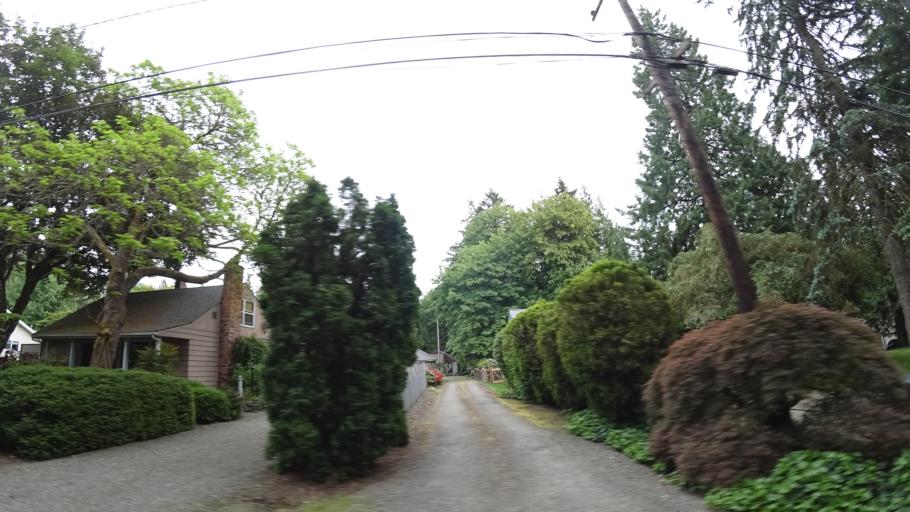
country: US
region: Oregon
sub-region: Washington County
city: West Slope
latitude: 45.4887
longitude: -122.7784
